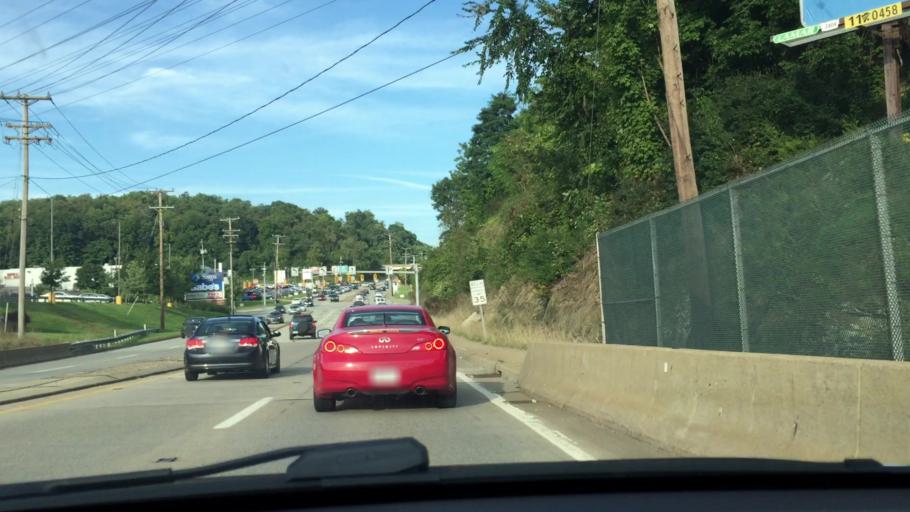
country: US
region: Pennsylvania
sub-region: Allegheny County
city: Monroeville
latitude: 40.4324
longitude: -79.8007
